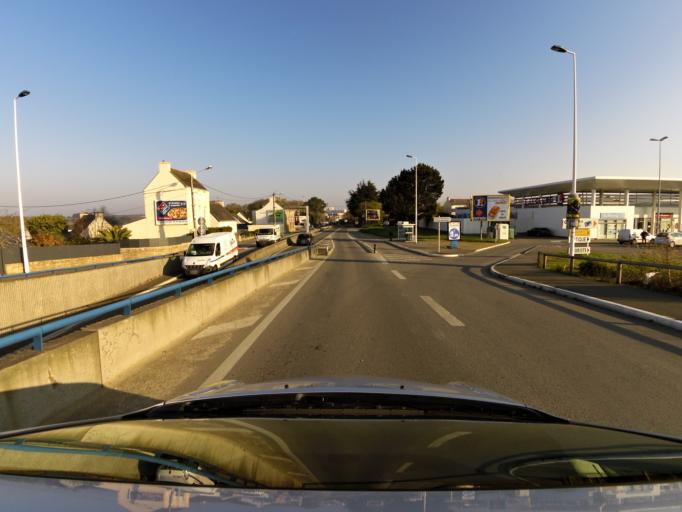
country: FR
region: Brittany
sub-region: Departement du Morbihan
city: Larmor-Plage
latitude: 47.7271
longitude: -3.3839
